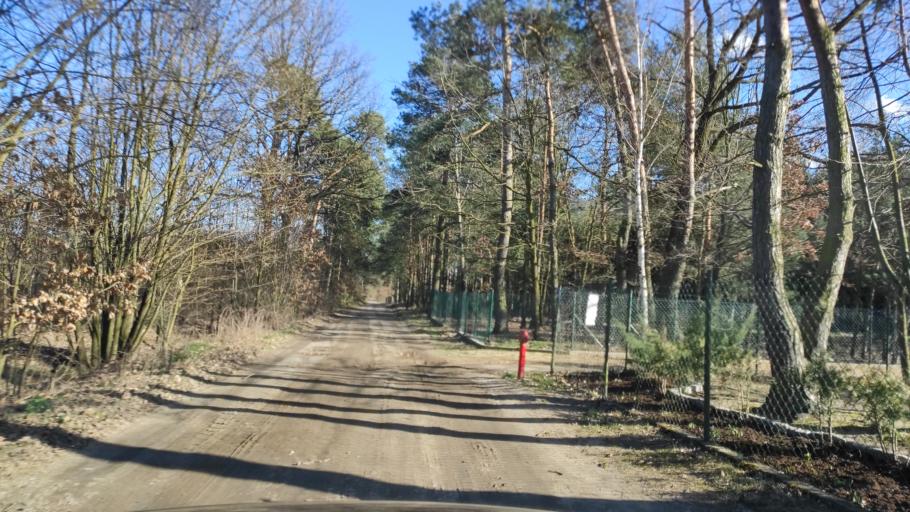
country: PL
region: Masovian Voivodeship
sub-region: Powiat radomski
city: Jastrzebia
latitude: 51.4548
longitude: 21.2749
